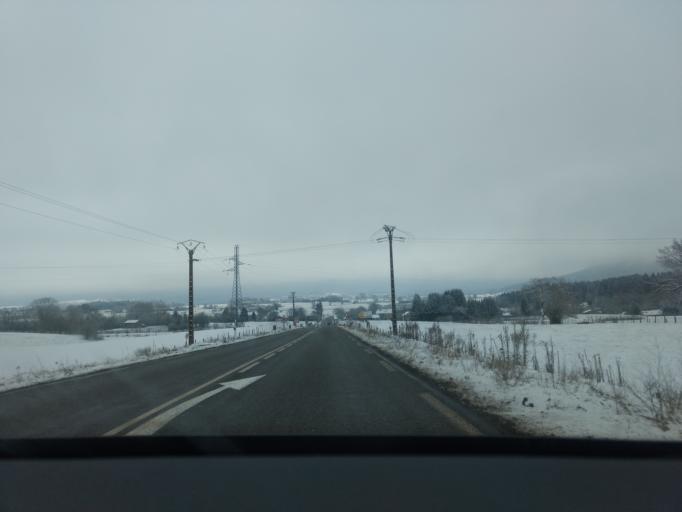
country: FR
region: Franche-Comte
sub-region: Departement du Jura
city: Champagnole
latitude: 46.7803
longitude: 5.8887
